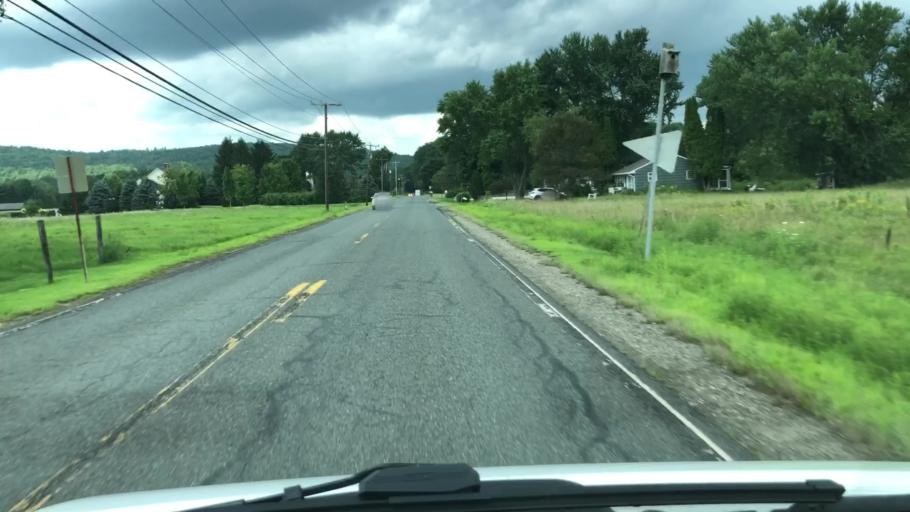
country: US
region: Massachusetts
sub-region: Franklin County
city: South Deerfield
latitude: 42.4890
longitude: -72.6263
